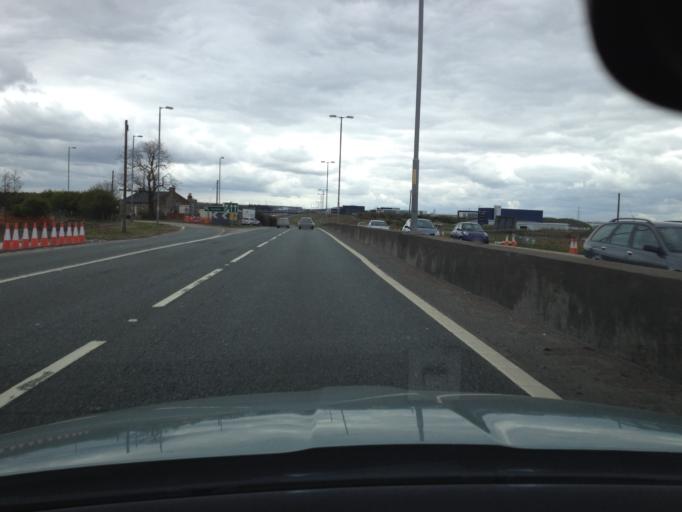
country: GB
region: Scotland
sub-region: North Lanarkshire
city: Bellshill
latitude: 55.8389
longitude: -4.0035
